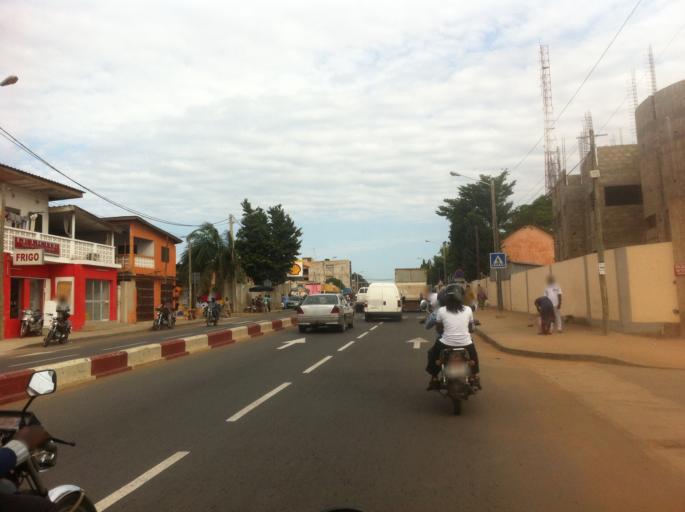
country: TG
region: Maritime
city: Lome
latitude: 6.1471
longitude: 1.2032
